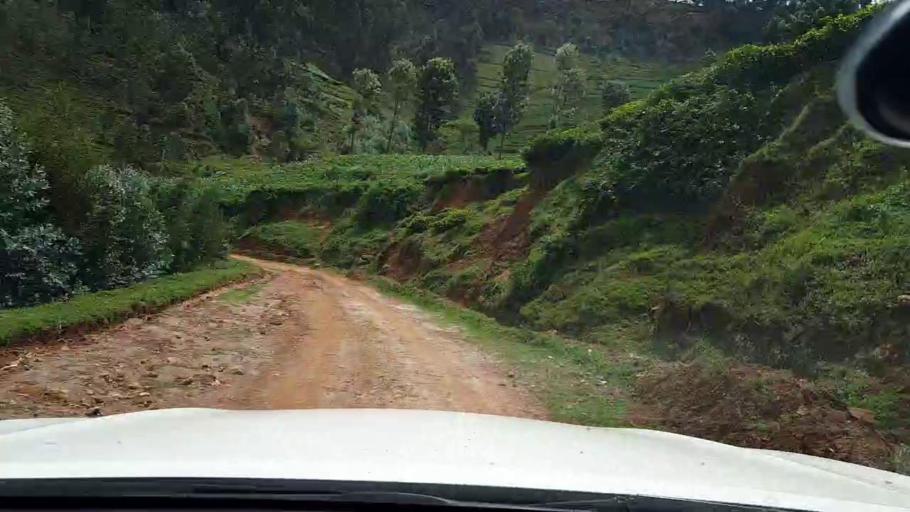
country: RW
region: Western Province
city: Kibuye
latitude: -2.1687
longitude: 29.3982
